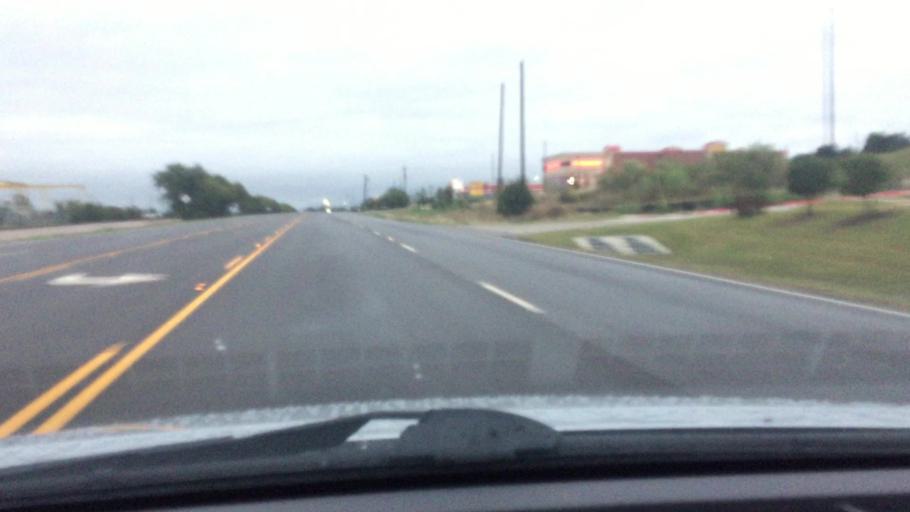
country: US
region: Texas
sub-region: Williamson County
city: Leander
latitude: 30.5657
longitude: -97.8475
